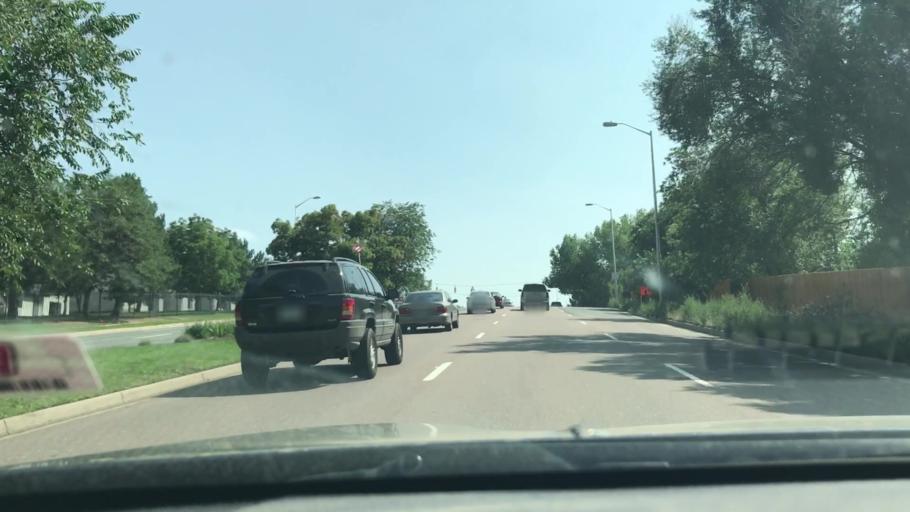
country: US
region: Colorado
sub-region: El Paso County
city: Cimarron Hills
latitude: 38.9274
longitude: -104.7753
